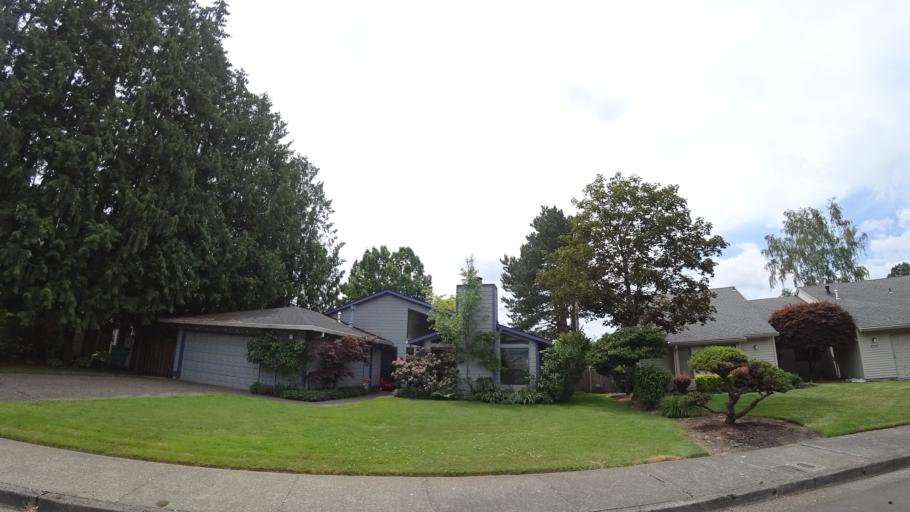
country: US
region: Oregon
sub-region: Washington County
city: Garden Home-Whitford
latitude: 45.4568
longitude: -122.7703
